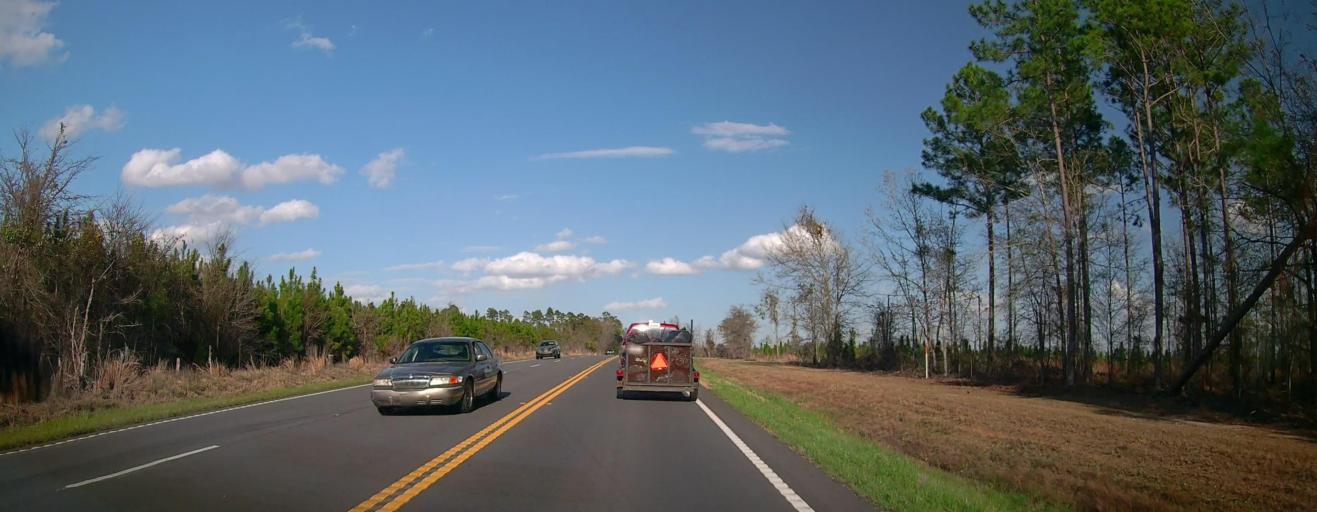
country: US
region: Georgia
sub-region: Montgomery County
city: Mount Vernon
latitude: 32.1908
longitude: -82.5214
